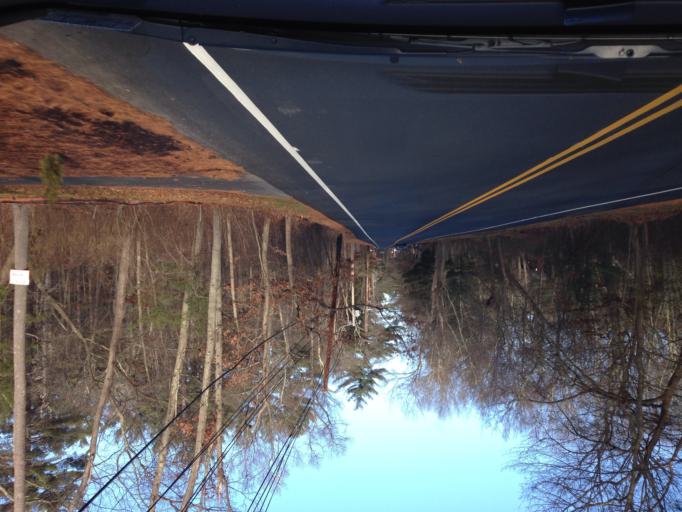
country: US
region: Massachusetts
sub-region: Middlesex County
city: Bedford
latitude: 42.5021
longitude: -71.2992
